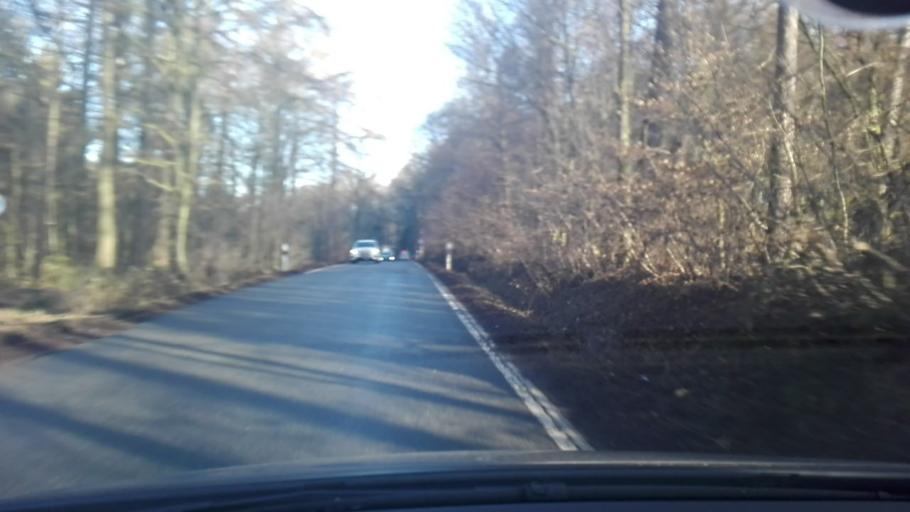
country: DE
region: North Rhine-Westphalia
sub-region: Regierungsbezirk Arnsberg
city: Frondenberg
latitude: 51.4838
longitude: 7.7594
